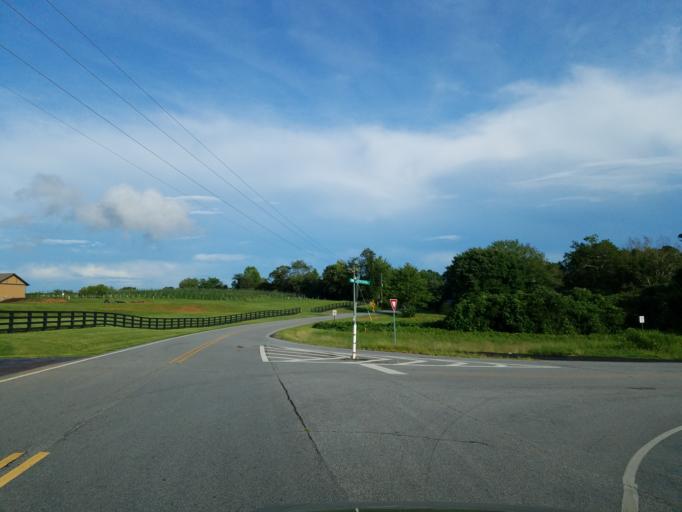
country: US
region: Georgia
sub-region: White County
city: Cleveland
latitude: 34.6072
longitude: -83.8597
